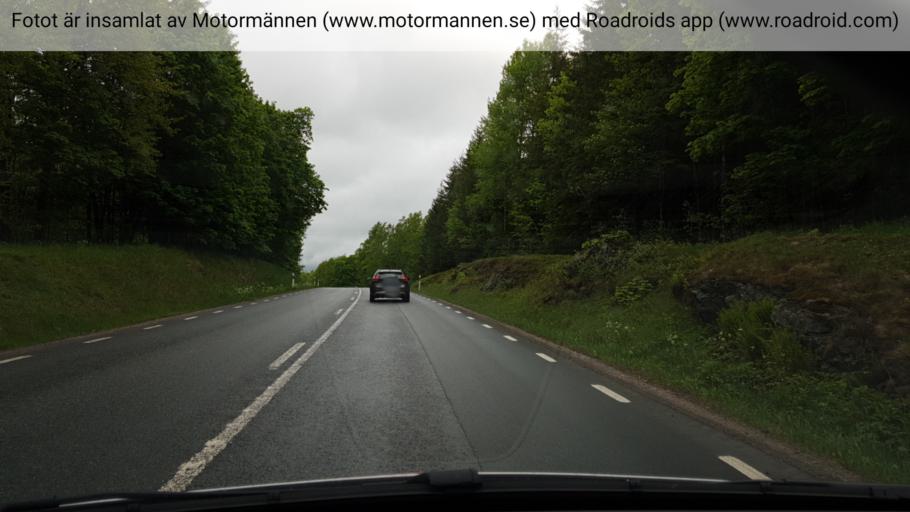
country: SE
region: Joenkoeping
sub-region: Aneby Kommun
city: Aneby
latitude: 57.8749
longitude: 14.8744
